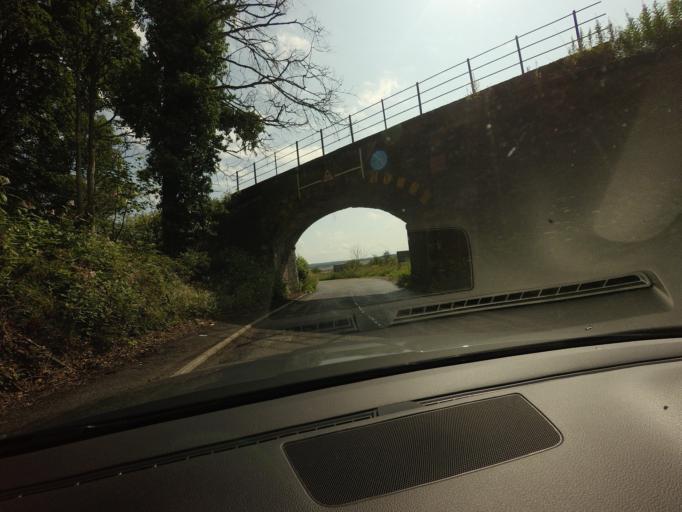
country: GB
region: Scotland
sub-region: Highland
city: Dingwall
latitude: 57.6092
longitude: -4.4111
